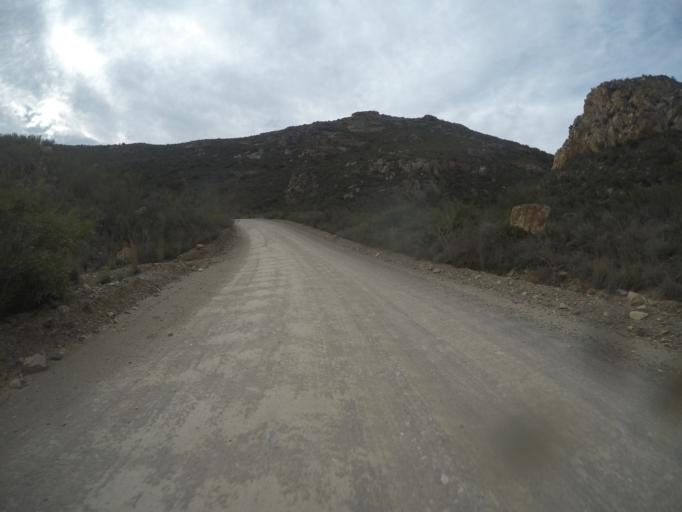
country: ZA
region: Eastern Cape
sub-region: Cacadu District Municipality
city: Willowmore
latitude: -33.5074
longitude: 23.6378
